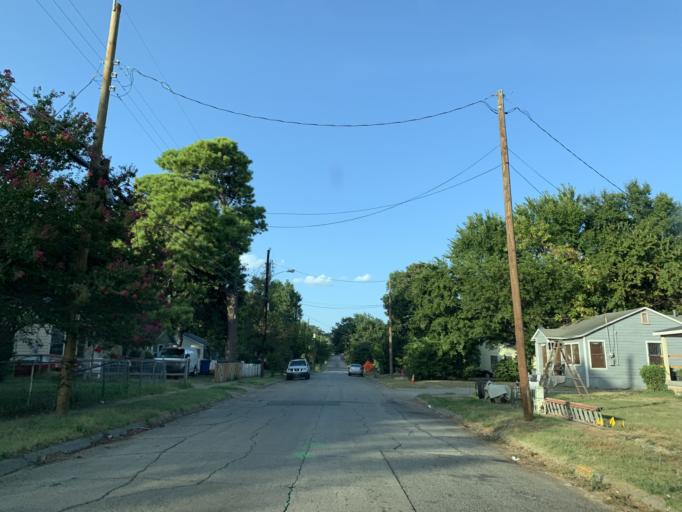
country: US
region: Texas
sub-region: Dallas County
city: Dallas
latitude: 32.7573
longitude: -96.7528
